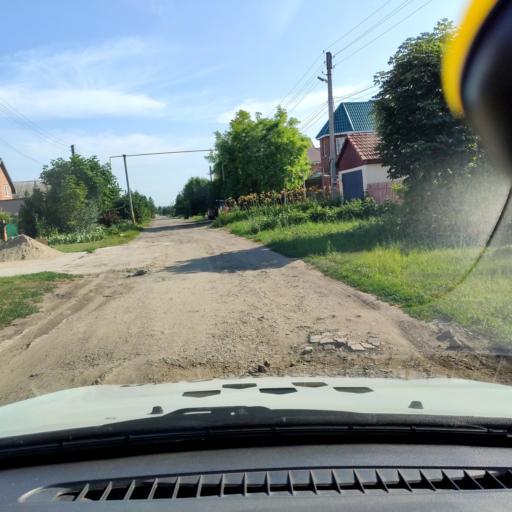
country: RU
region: Samara
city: Podstepki
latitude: 53.5212
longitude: 49.1906
